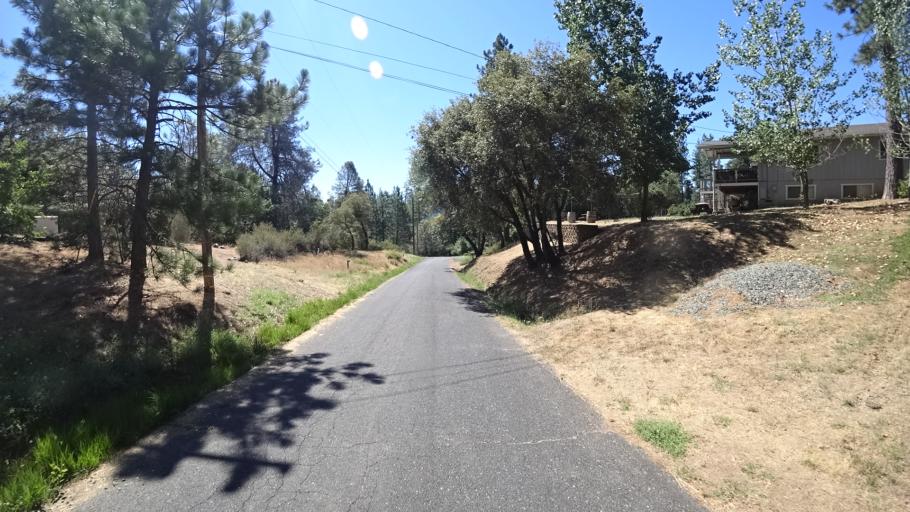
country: US
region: California
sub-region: Calaveras County
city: Forest Meadows
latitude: 38.1832
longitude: -120.3650
